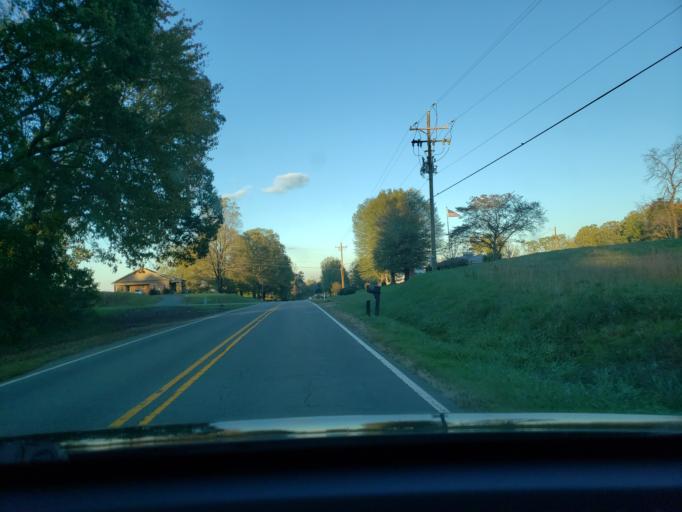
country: US
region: North Carolina
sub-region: Stokes County
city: Danbury
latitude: 36.3591
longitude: -80.2109
